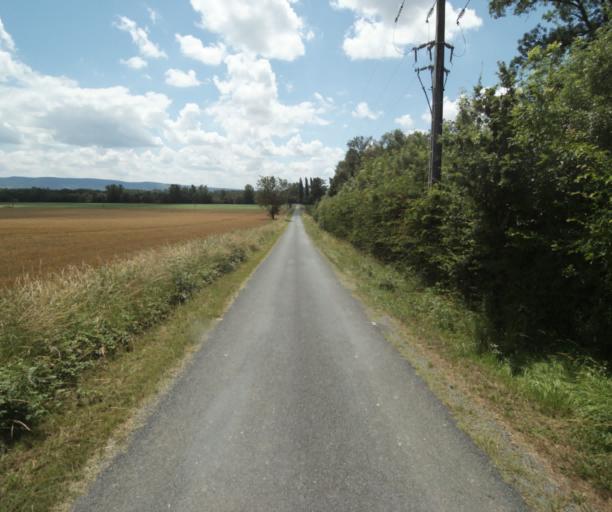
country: FR
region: Midi-Pyrenees
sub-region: Departement du Tarn
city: Puylaurens
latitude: 43.5238
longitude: 2.0245
